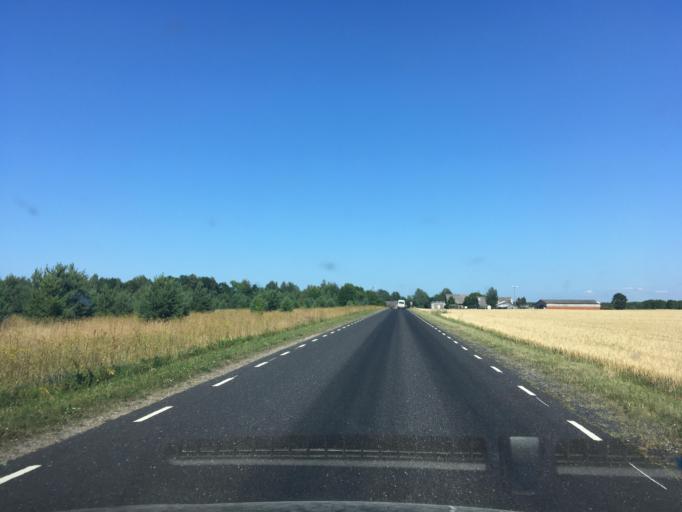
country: EE
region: Harju
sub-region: Anija vald
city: Kehra
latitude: 59.1763
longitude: 25.2192
